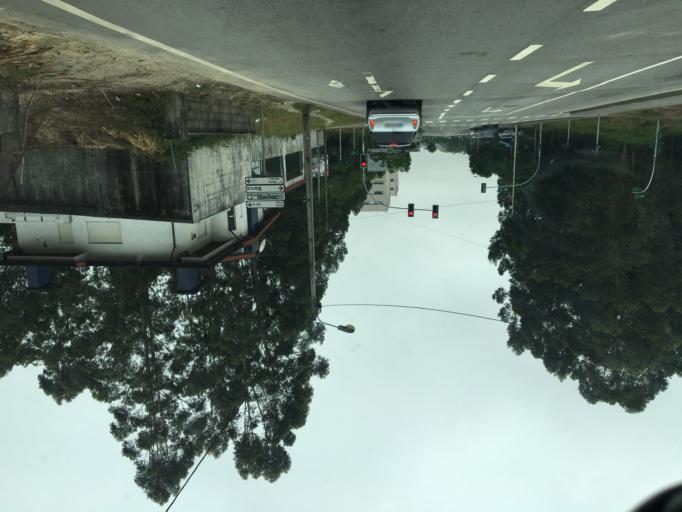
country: PT
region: Porto
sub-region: Maia
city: Anta
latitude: 41.2599
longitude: -8.6079
